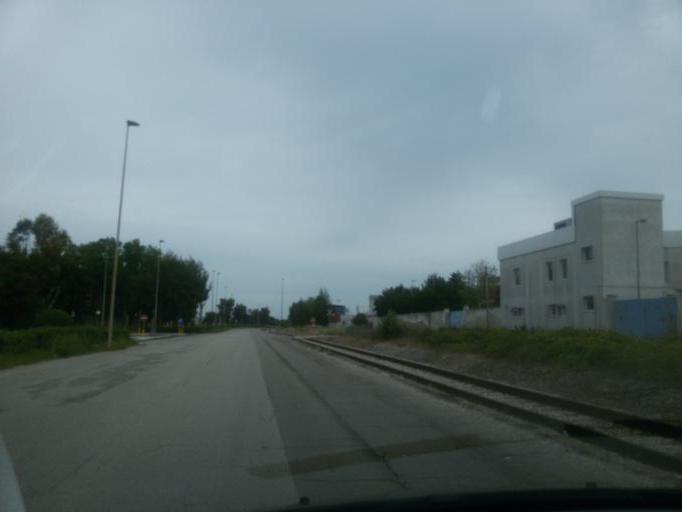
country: IT
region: Apulia
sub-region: Provincia di Brindisi
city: Materdomini
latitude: 40.6389
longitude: 17.9783
